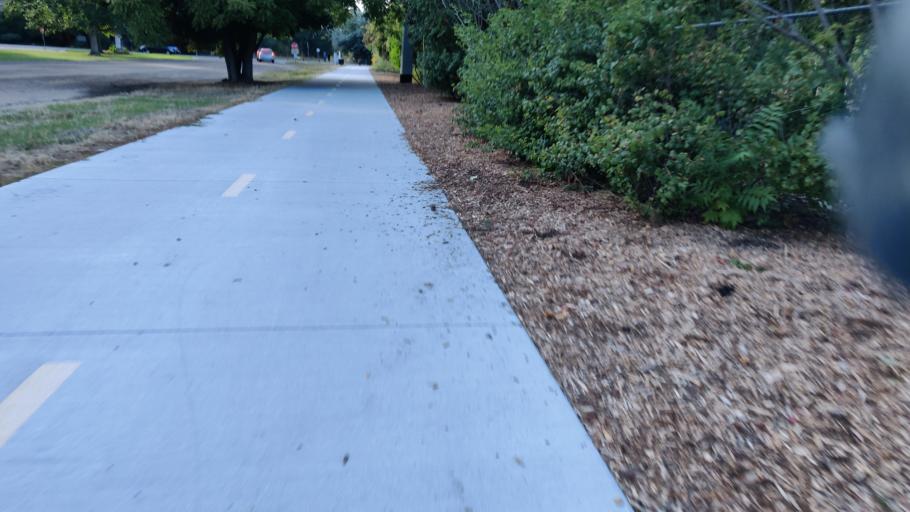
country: US
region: Idaho
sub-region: Ada County
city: Boise
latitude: 43.6038
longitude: -116.1837
